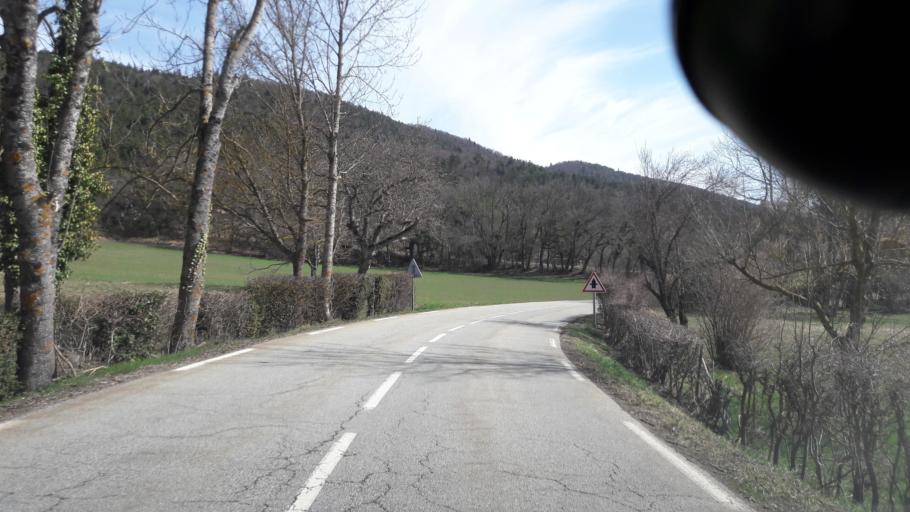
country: FR
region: Rhone-Alpes
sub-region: Departement de l'Isere
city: La Motte-Saint-Martin
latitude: 44.8861
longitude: 5.6406
